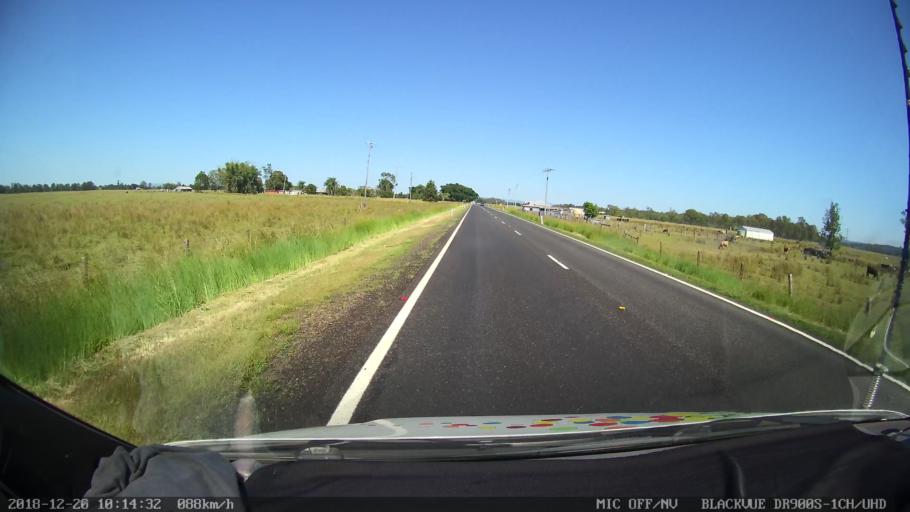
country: AU
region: New South Wales
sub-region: Richmond Valley
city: Casino
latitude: -28.8697
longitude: 153.1133
